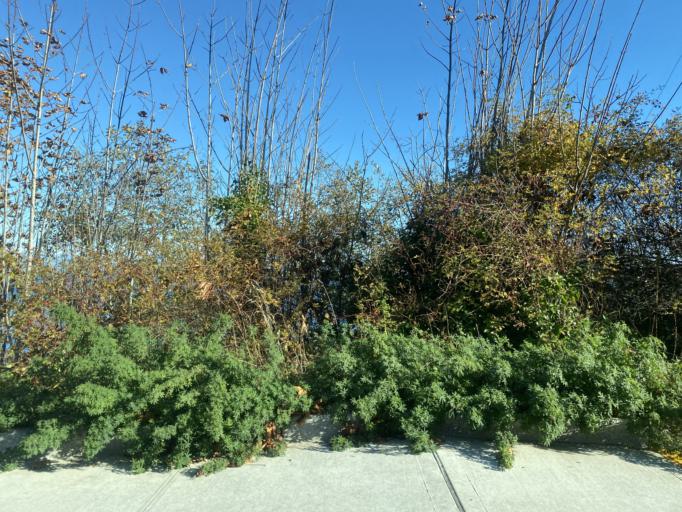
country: US
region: Washington
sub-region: Snohomish County
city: Mukilteo
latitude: 47.9737
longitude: -122.3521
